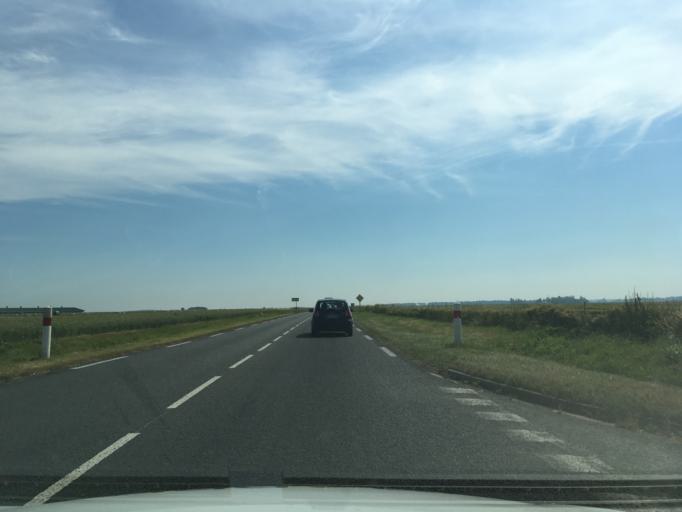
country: FR
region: Picardie
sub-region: Departement de la Somme
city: Montdidier
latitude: 49.6473
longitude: 2.6276
